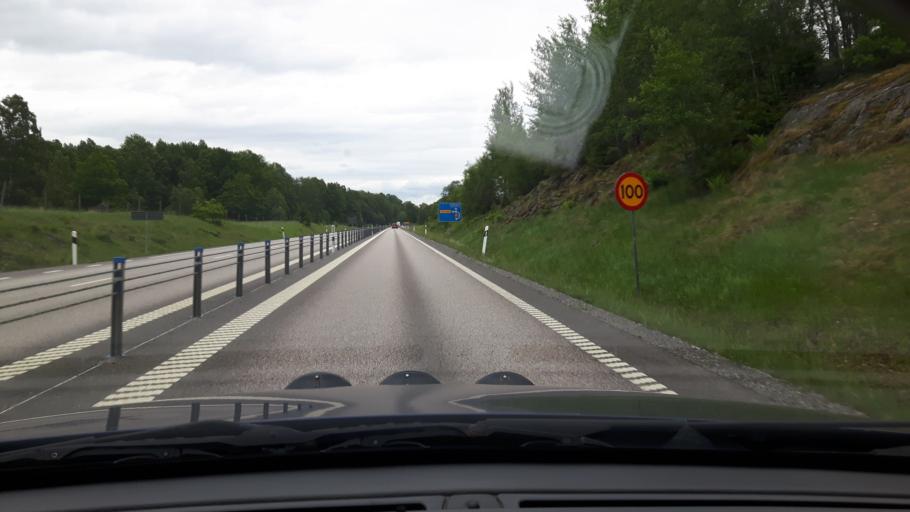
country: SE
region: Soedermanland
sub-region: Flens Kommun
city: Flen
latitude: 59.0401
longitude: 16.5027
